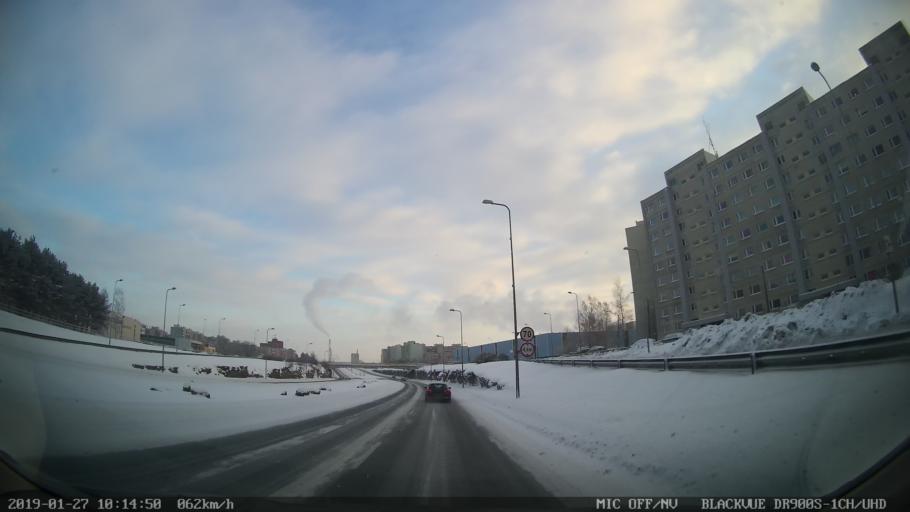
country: EE
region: Harju
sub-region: Tallinna linn
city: Kose
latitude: 59.4430
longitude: 24.8783
